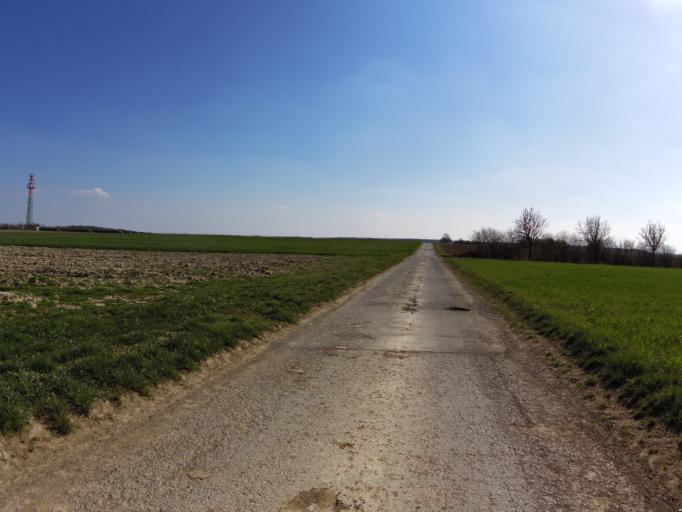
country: DE
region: Bavaria
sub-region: Regierungsbezirk Unterfranken
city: Biebelried
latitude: 49.7409
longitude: 10.1013
